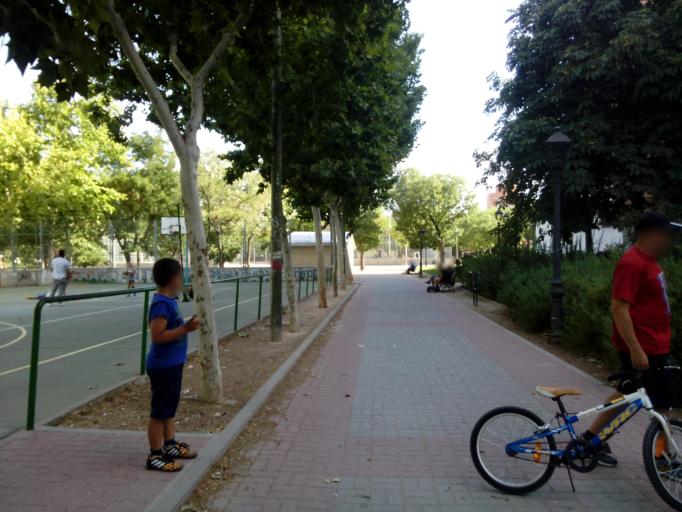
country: ES
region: Madrid
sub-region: Provincia de Madrid
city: Carabanchel
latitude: 40.3936
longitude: -3.7149
